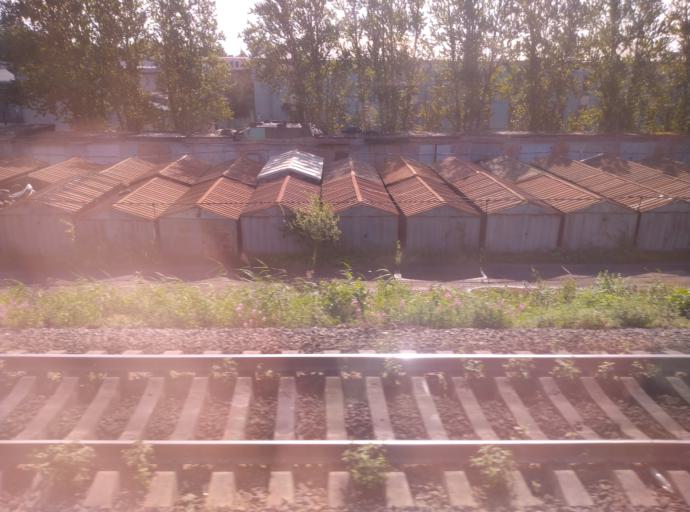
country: RU
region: St.-Petersburg
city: Centralniy
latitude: 59.9096
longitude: 30.3898
